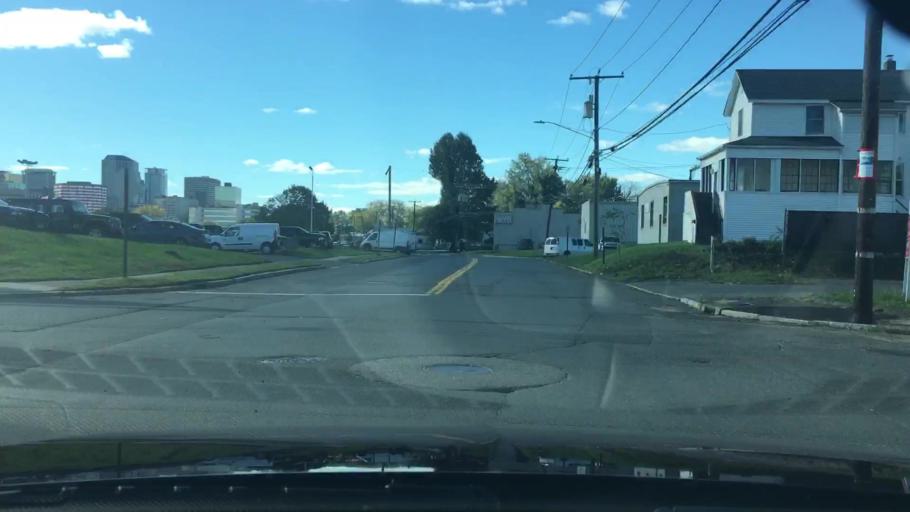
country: US
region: Connecticut
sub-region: Hartford County
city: Hartford
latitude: 41.7711
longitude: -72.6535
